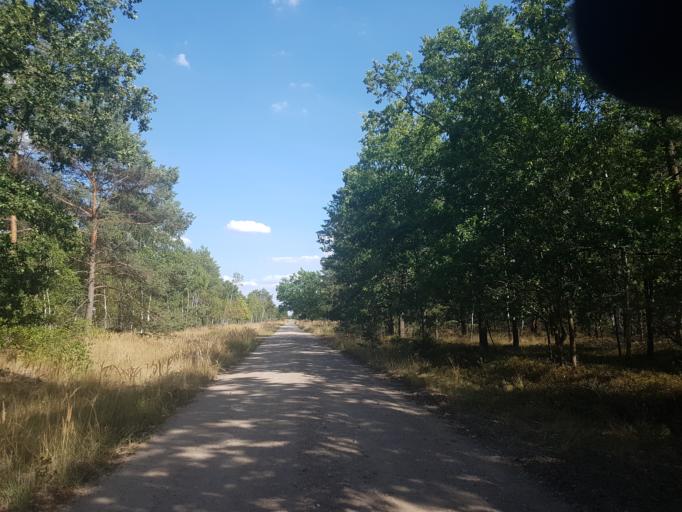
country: DE
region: Saxony-Anhalt
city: Seyda
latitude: 51.8760
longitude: 12.9610
